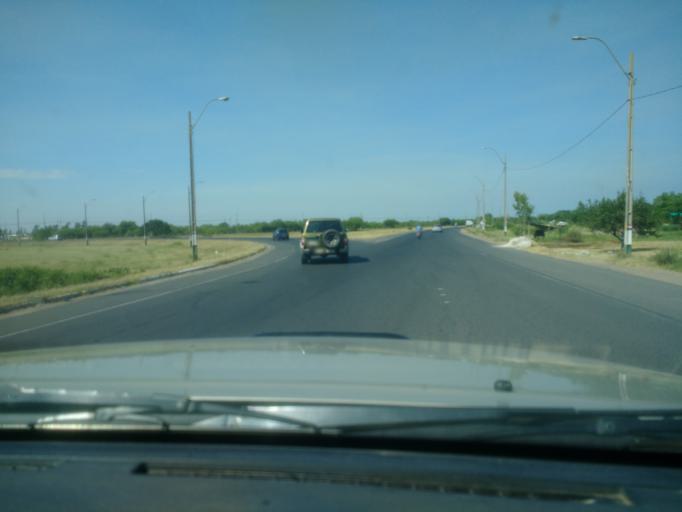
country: PY
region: Central
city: Colonia Mariano Roque Alonso
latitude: -25.1696
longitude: -57.5641
